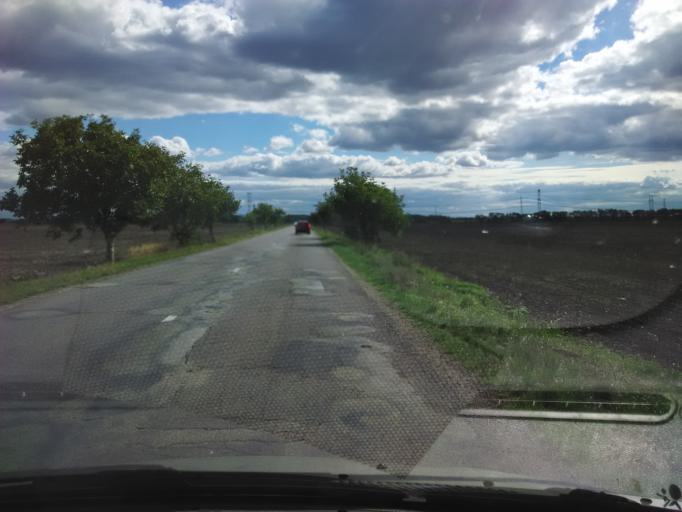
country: SK
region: Nitriansky
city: Tlmace
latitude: 48.2196
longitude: 18.5015
